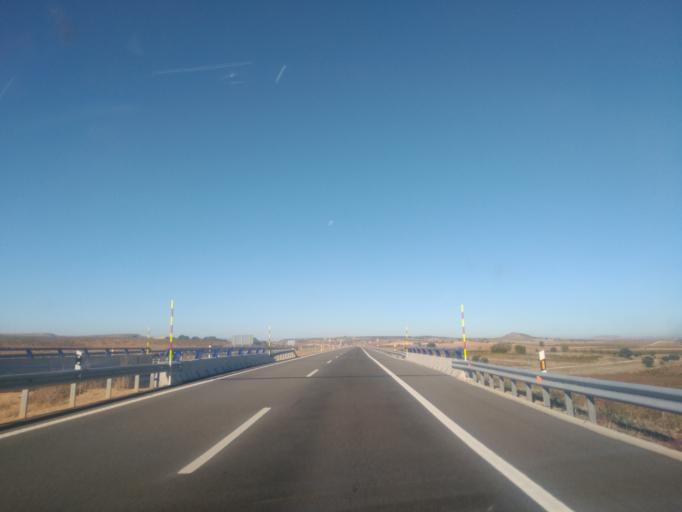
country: ES
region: Castille and Leon
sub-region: Provincia de Burgos
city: Castrillo de la Vega
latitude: 41.6343
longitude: -3.7670
